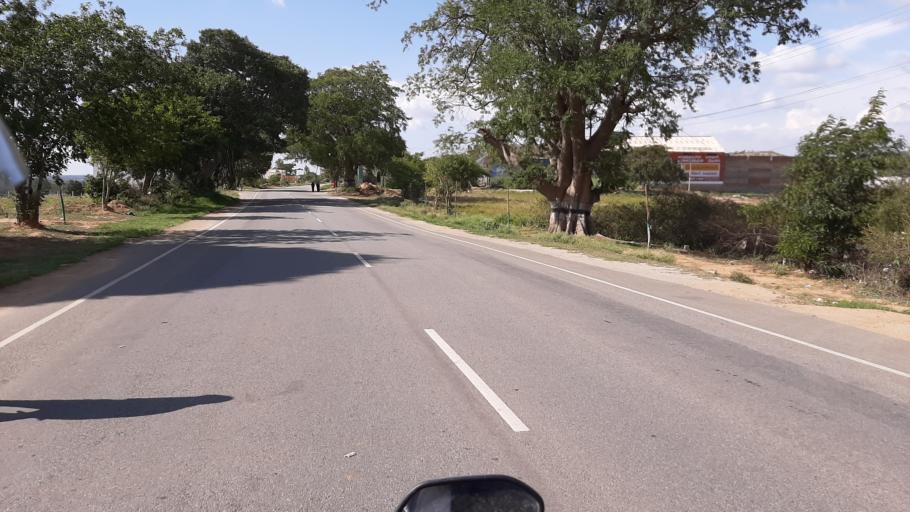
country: IN
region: Tamil Nadu
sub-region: Krishnagiri
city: Denkanikota
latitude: 12.5516
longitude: 77.7860
